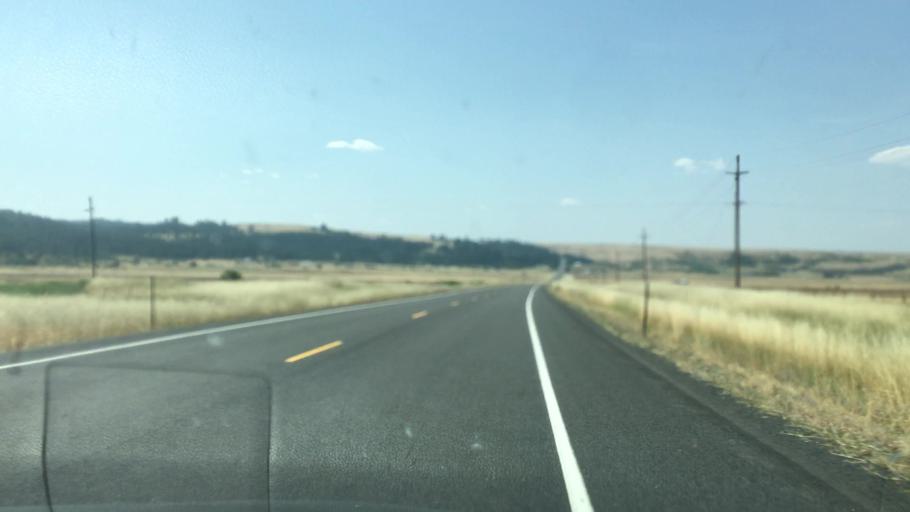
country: US
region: Idaho
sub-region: Idaho County
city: Grangeville
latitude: 45.8888
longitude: -116.2010
